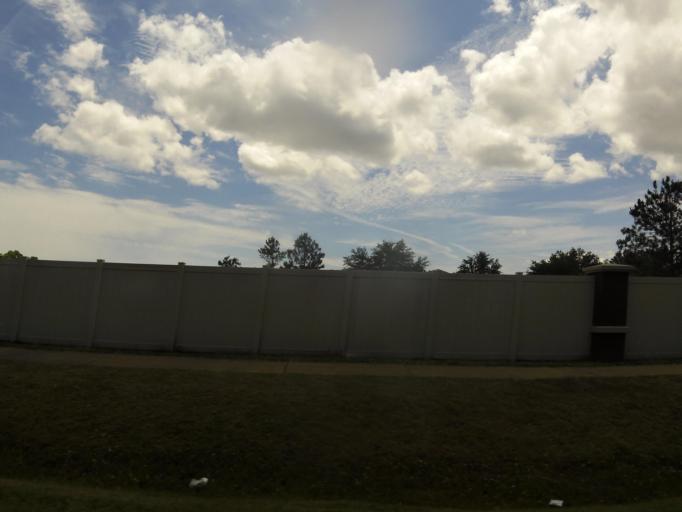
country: US
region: Florida
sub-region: Duval County
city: Jacksonville
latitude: 30.4717
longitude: -81.6104
